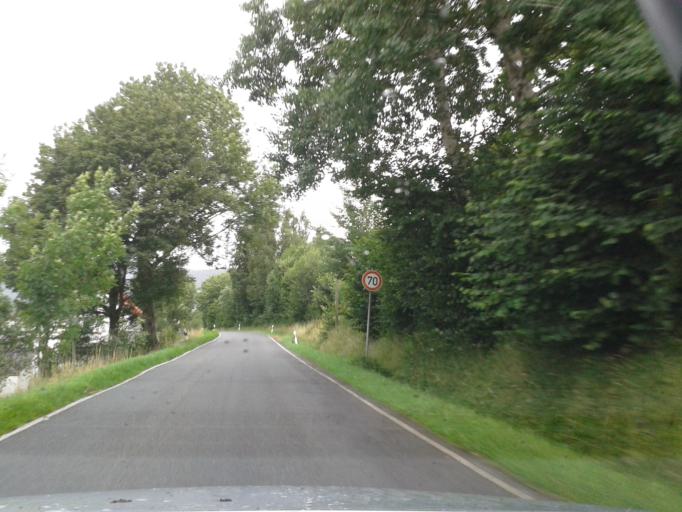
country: DE
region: North Rhine-Westphalia
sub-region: Regierungsbezirk Detmold
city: Lugde
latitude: 51.9508
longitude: 9.2261
